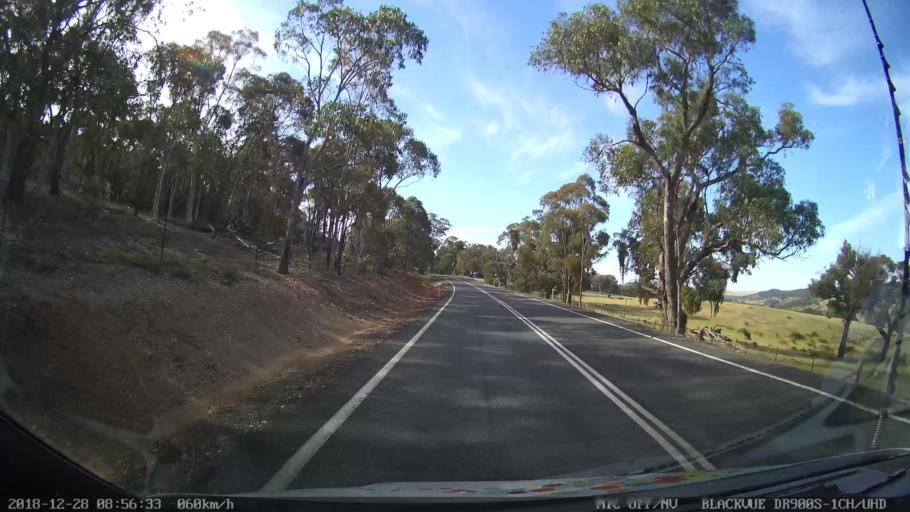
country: AU
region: New South Wales
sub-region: Upper Lachlan Shire
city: Crookwell
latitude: -34.1113
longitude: 149.3377
